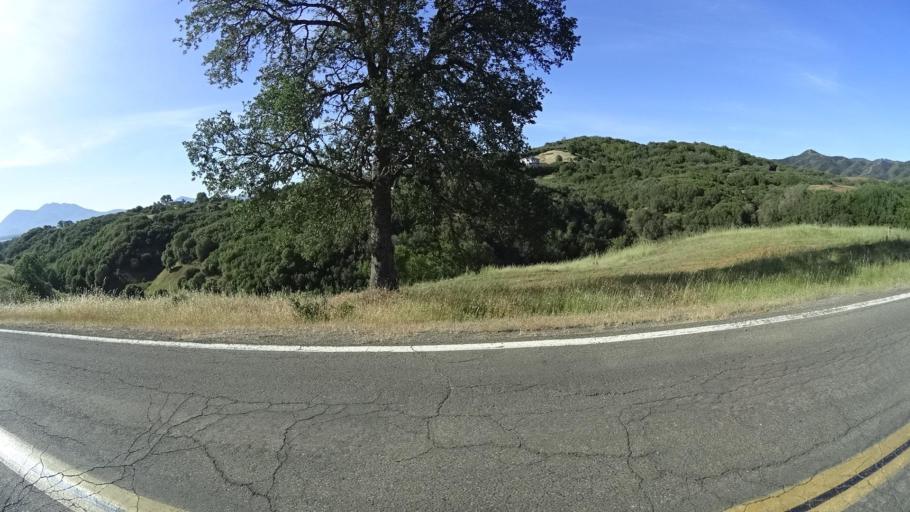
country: US
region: California
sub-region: Lake County
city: Lakeport
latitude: 39.0411
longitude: -122.9483
